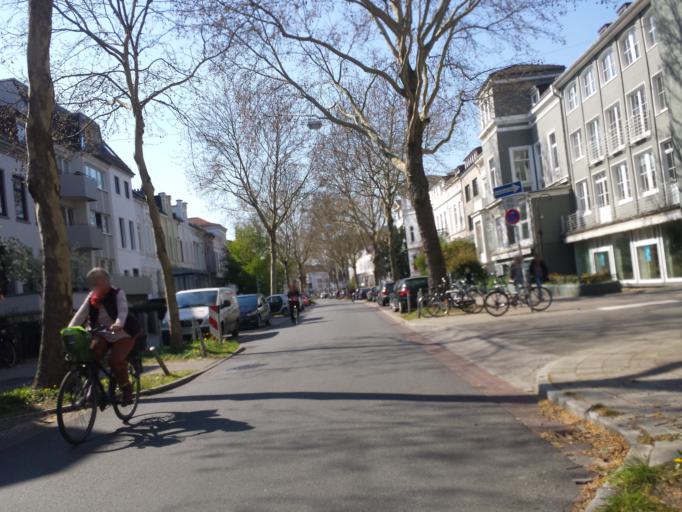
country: DE
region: Bremen
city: Bremen
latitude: 53.0750
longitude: 8.8257
